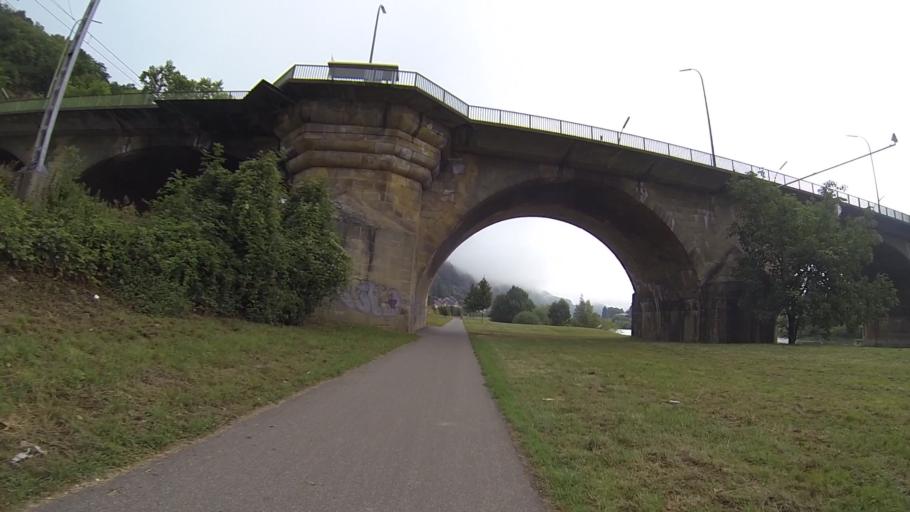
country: DE
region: Rheinland-Pfalz
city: Trier
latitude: 49.7646
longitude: 6.6308
